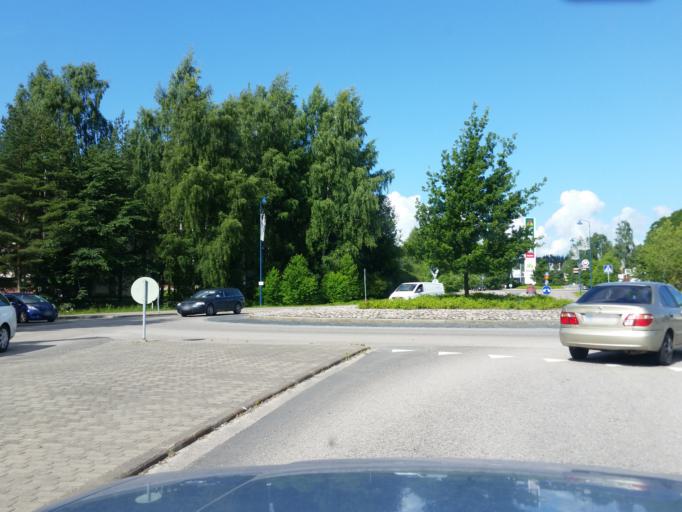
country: FI
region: Uusimaa
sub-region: Helsinki
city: Vihti
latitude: 60.3320
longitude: 24.3277
